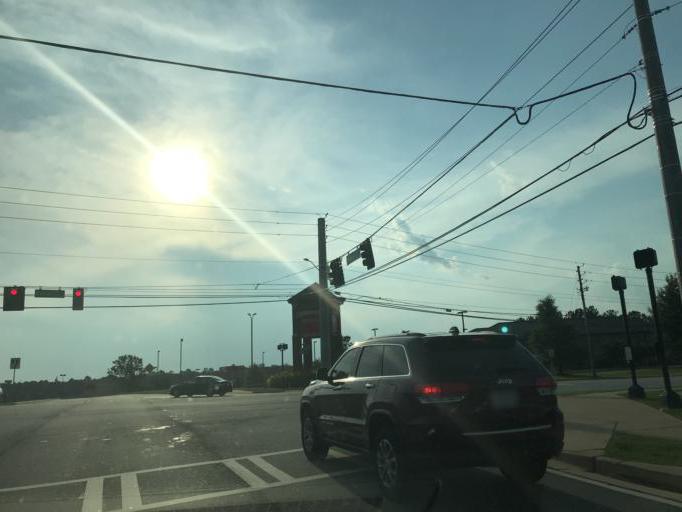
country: US
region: Alabama
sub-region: Russell County
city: Phenix City
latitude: 32.5395
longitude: -84.9661
